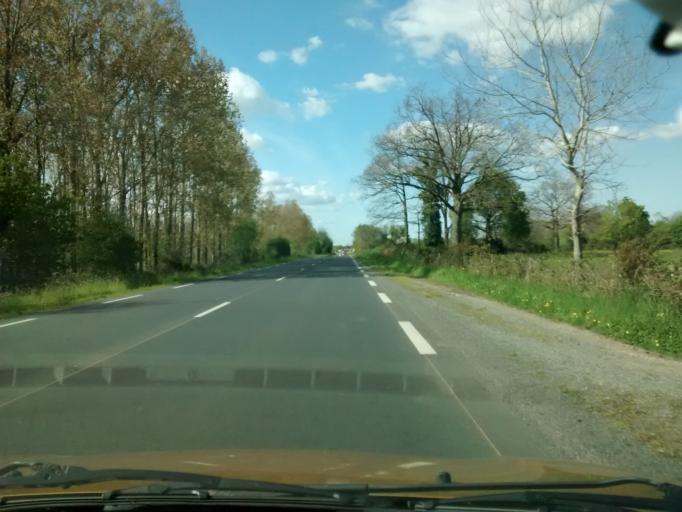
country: FR
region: Pays de la Loire
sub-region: Departement de la Loire-Atlantique
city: Geneston
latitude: 47.0417
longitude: -1.5076
